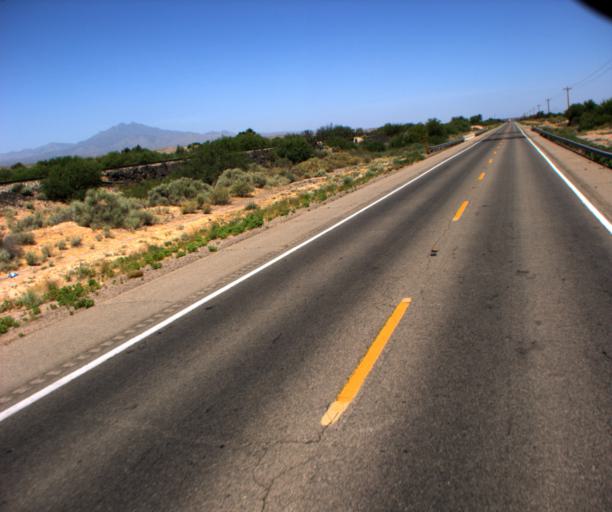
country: US
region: Arizona
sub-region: Graham County
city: Bylas
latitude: 33.0482
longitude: -109.9872
